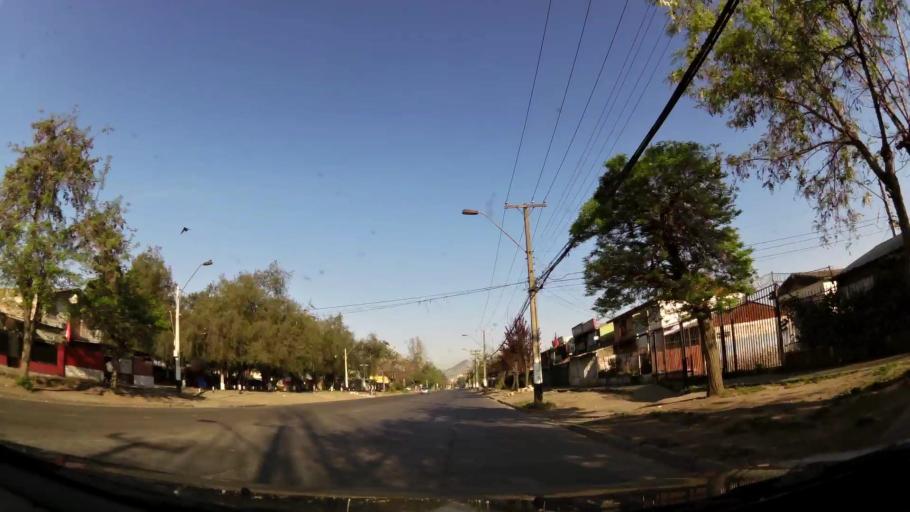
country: CL
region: Santiago Metropolitan
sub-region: Provincia de Santiago
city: Santiago
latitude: -33.3867
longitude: -70.6582
